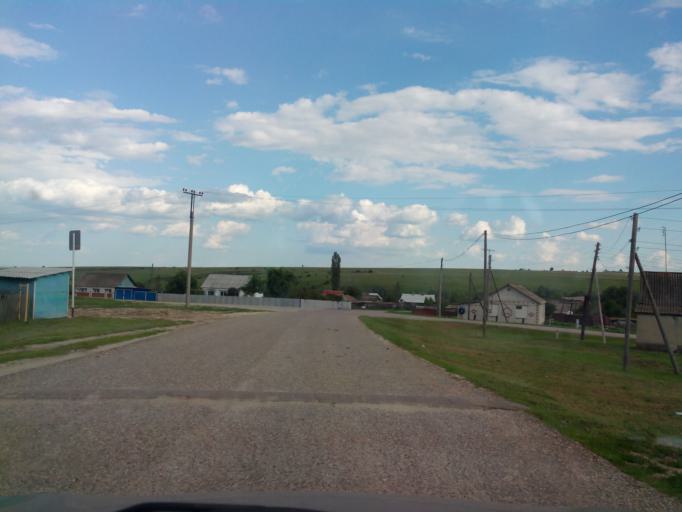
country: RU
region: Volgograd
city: Slashchevskaya
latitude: 49.7782
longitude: 42.4406
